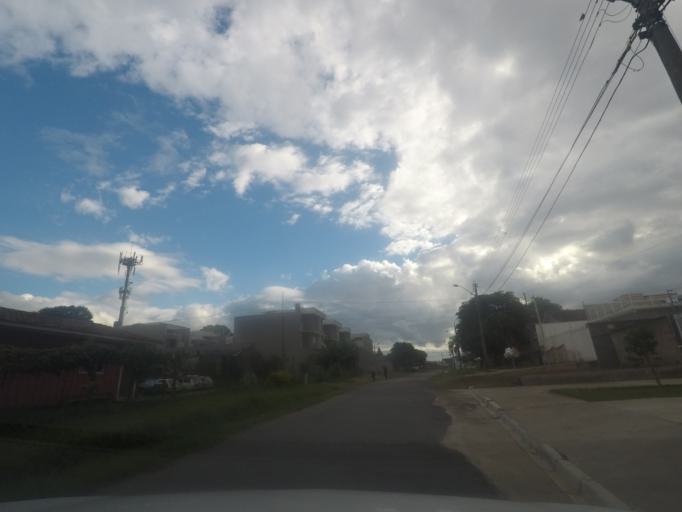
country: BR
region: Parana
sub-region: Pinhais
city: Pinhais
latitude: -25.4693
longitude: -49.2174
